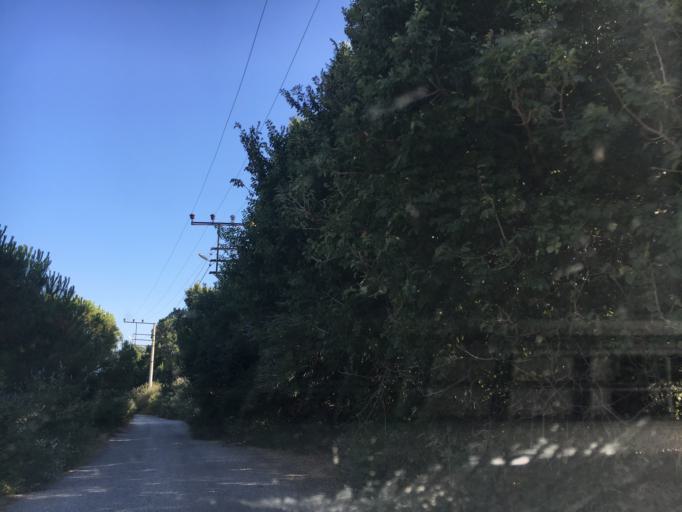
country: TR
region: Canakkale
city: Behram
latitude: 39.4814
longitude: 26.2567
